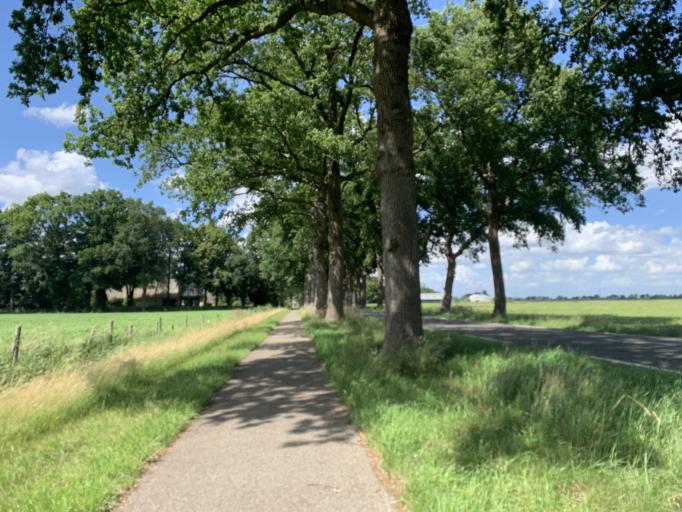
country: NL
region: Drenthe
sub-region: Gemeente Tynaarlo
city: Zuidlaren
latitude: 53.1369
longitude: 6.6538
